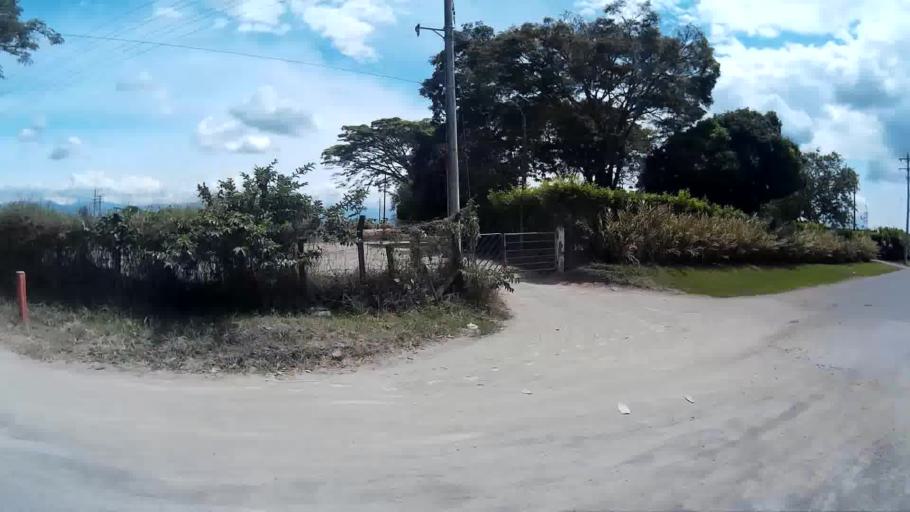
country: CO
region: Risaralda
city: Pereira
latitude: 4.8128
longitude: -75.8071
